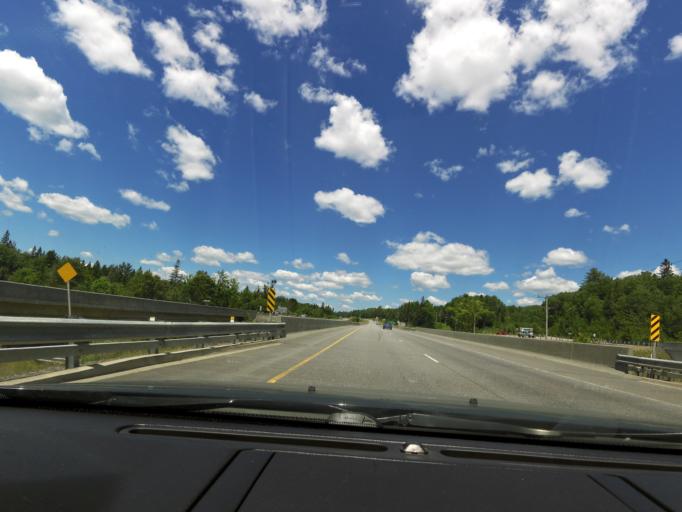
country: CA
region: Ontario
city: Huntsville
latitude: 45.3790
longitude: -79.2222
